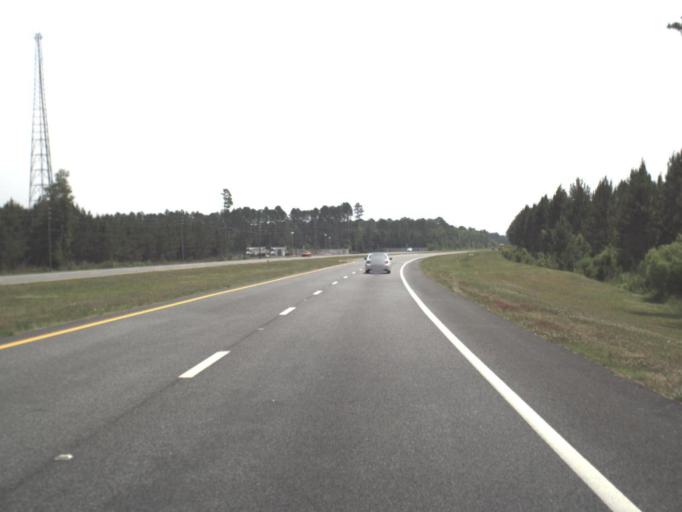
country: US
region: Florida
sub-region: Nassau County
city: Callahan
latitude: 30.6092
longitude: -81.7400
